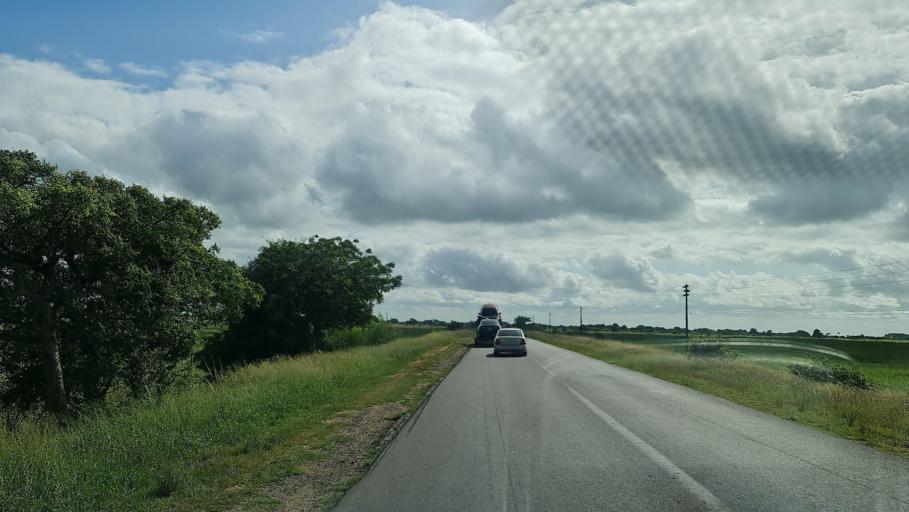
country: MZ
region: Gaza
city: Macia
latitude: -25.0958
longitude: 32.8313
